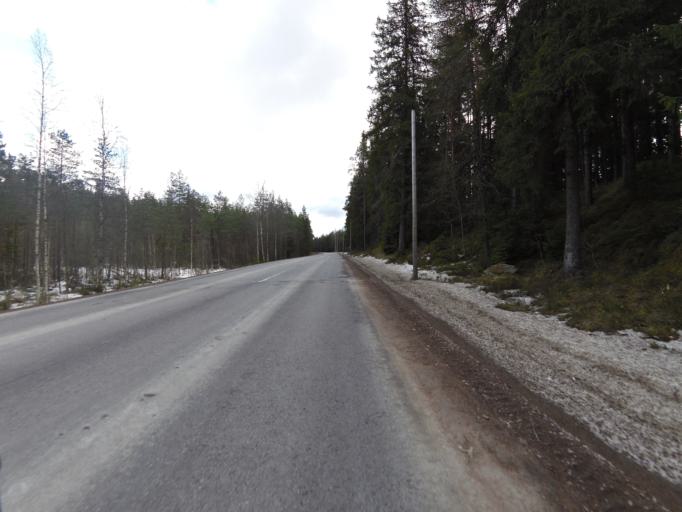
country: SE
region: Dalarna
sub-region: Hedemora Kommun
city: Brunna
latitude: 60.3106
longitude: 16.1633
